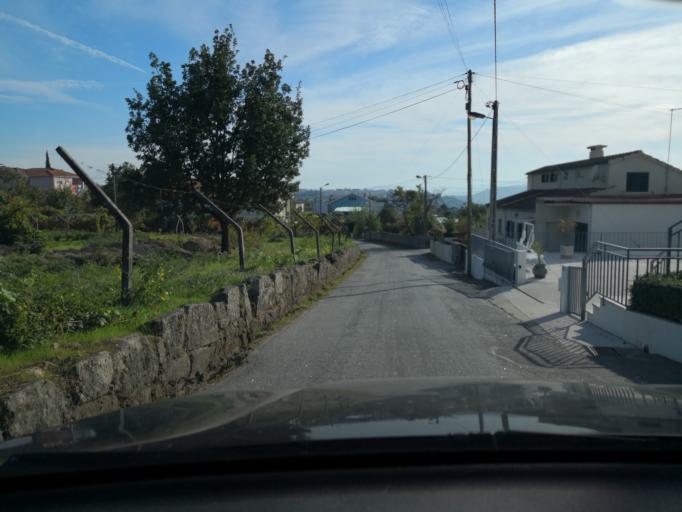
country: PT
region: Vila Real
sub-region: Vila Real
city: Vila Real
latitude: 41.3296
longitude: -7.7417
